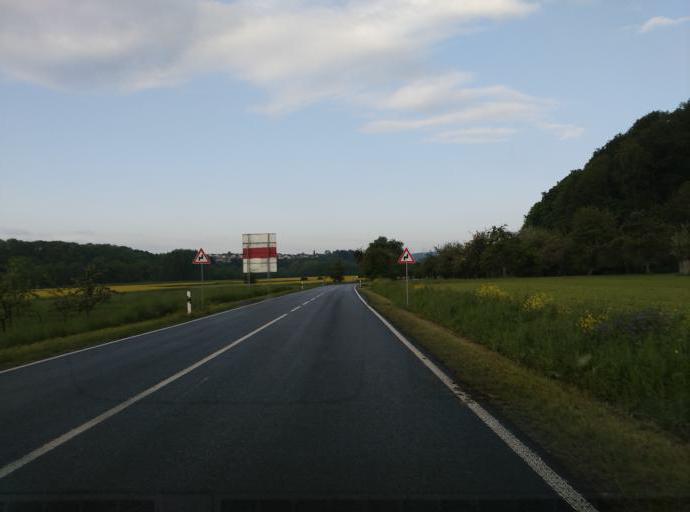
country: DE
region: Baden-Wuerttemberg
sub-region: Regierungsbezirk Stuttgart
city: Neckartailfingen
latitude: 48.6035
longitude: 9.2536
